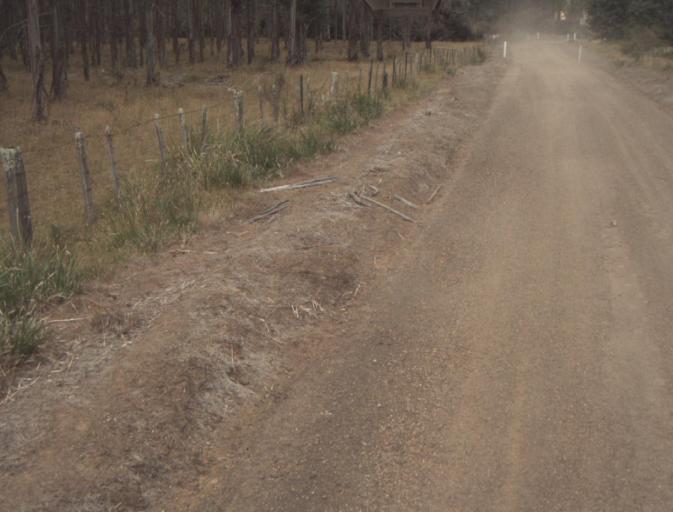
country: AU
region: Tasmania
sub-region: Dorset
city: Scottsdale
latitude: -41.4088
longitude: 147.5298
